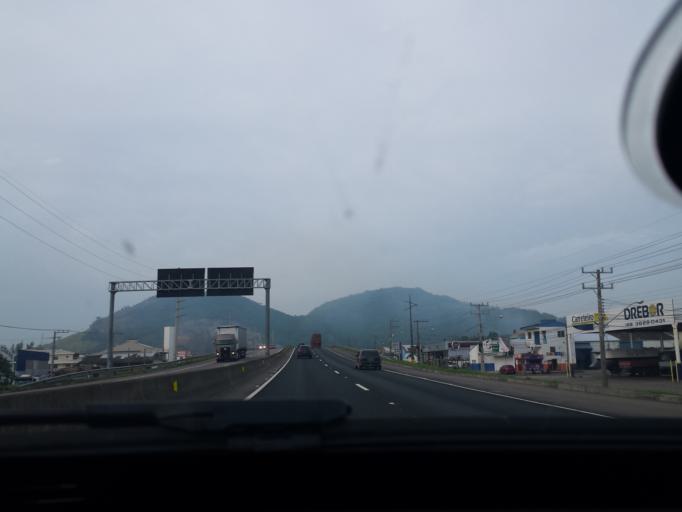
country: BR
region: Santa Catarina
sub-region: Tubarao
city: Tubarao
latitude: -28.4751
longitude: -49.0277
